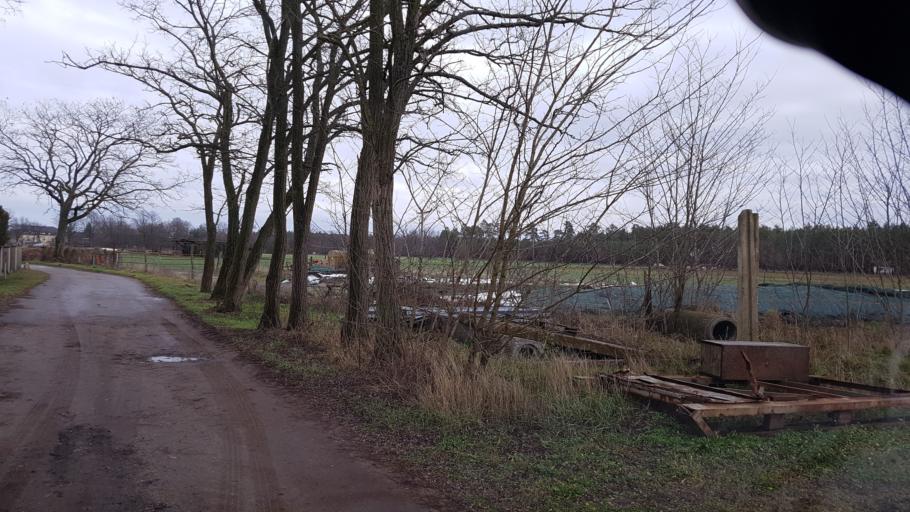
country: DE
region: Brandenburg
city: Altdobern
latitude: 51.6809
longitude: 14.0177
